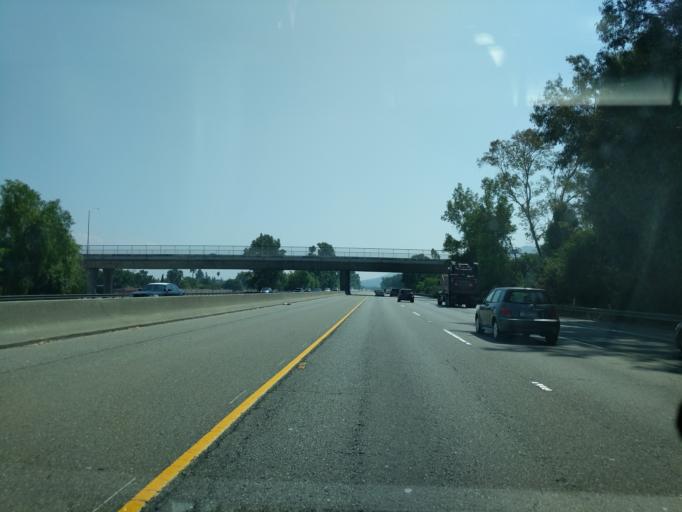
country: US
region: California
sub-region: Alameda County
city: Dublin
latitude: 37.6790
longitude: -121.9141
